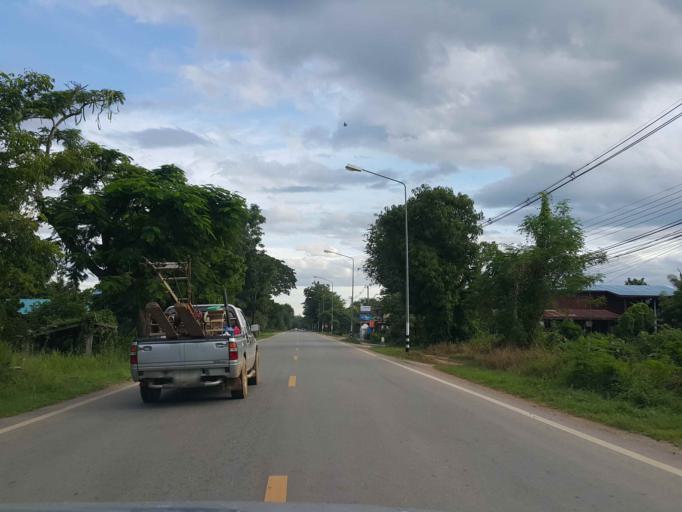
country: TH
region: Sukhothai
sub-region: Amphoe Si Satchanalai
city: Si Satchanalai
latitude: 17.5068
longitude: 99.7531
